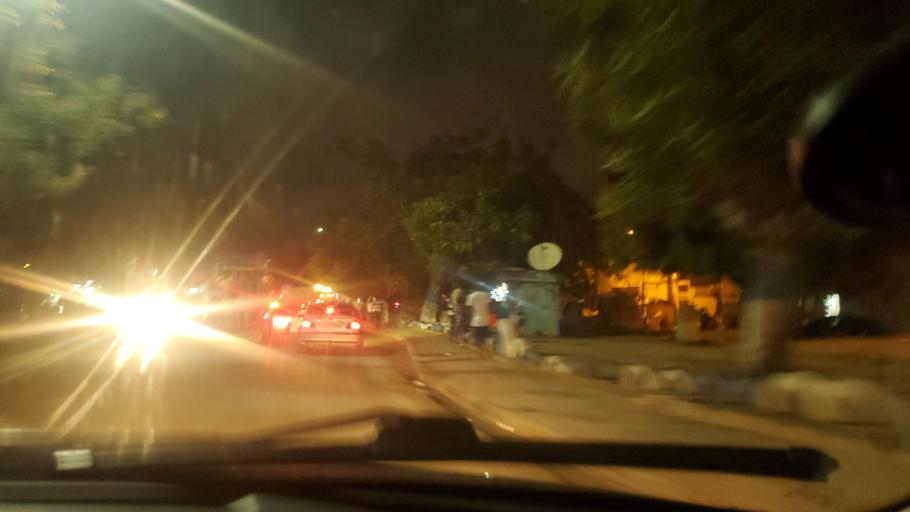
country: SN
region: Dakar
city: Grand Dakar
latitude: 14.7258
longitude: -17.4448
